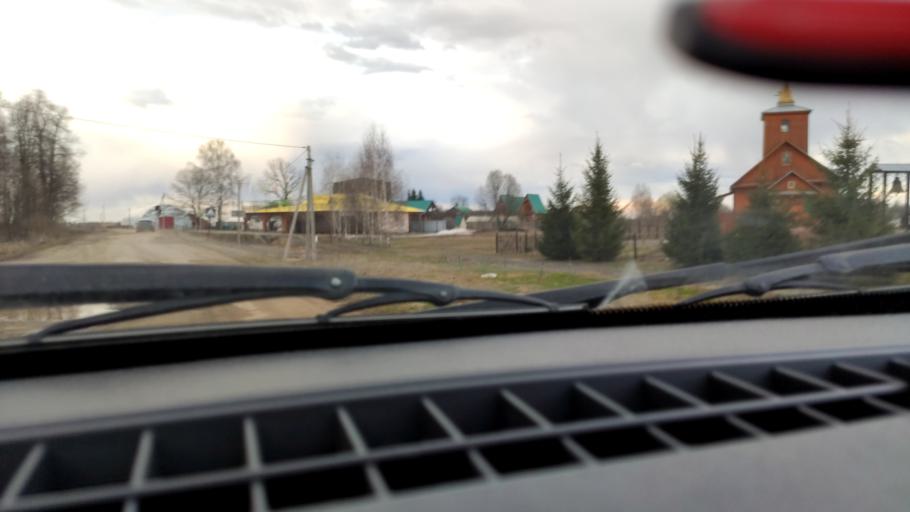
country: RU
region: Bashkortostan
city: Kudeyevskiy
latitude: 54.8132
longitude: 56.7533
